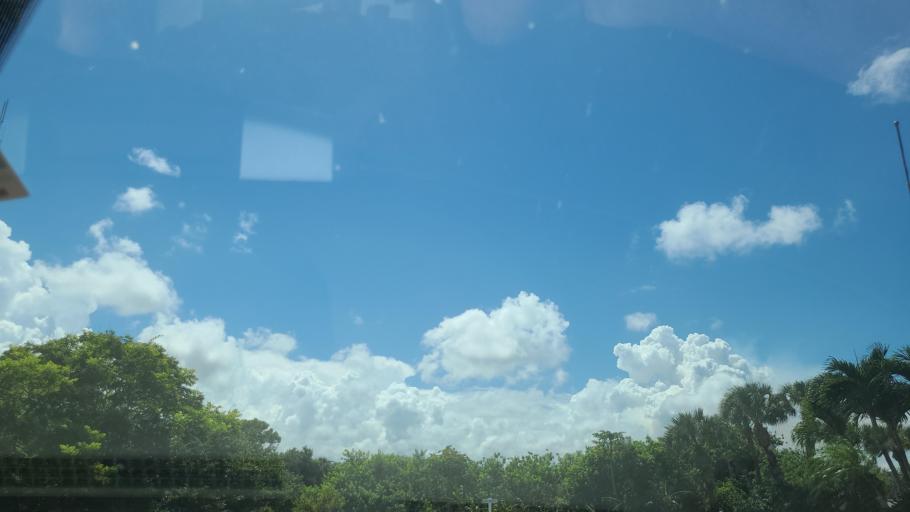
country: US
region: Florida
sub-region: Indian River County
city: Sebastian
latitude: 27.7884
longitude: -80.4636
